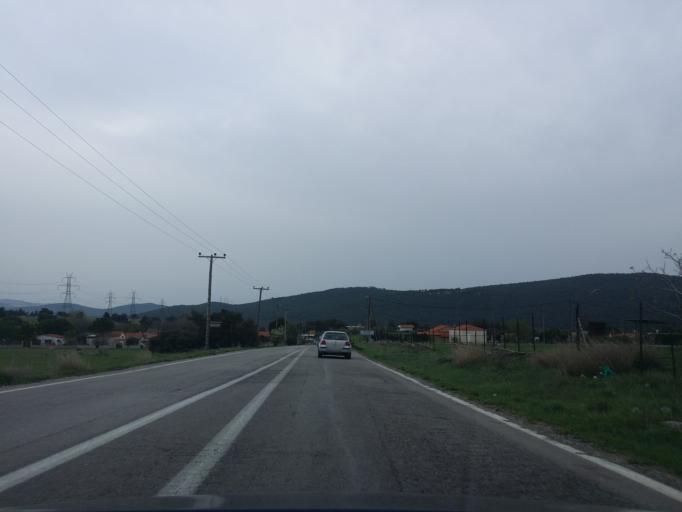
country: GR
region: Attica
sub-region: Nomarchia Dytikis Attikis
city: Vilia
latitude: 38.1747
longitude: 23.3837
